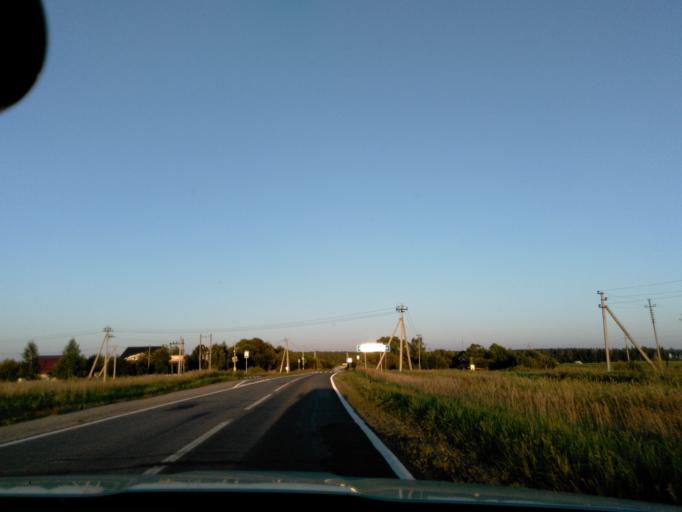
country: RU
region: Moskovskaya
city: Solnechnogorsk
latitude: 56.1188
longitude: 36.9111
